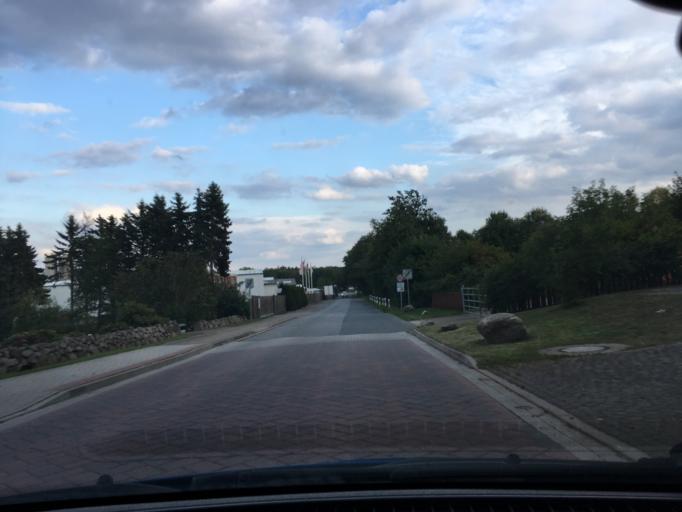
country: DE
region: Lower Saxony
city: Garstedt
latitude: 53.2842
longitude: 10.1653
